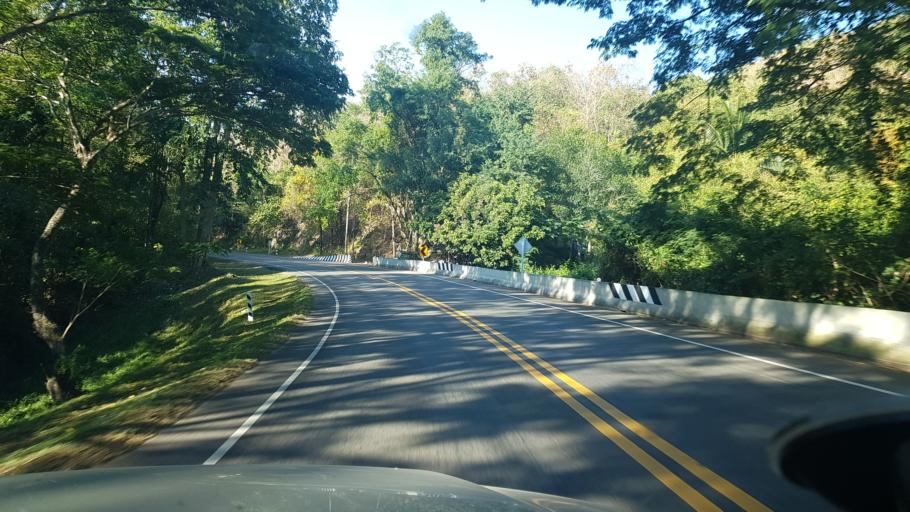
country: TH
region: Phetchabun
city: Lom Sak
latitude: 16.7477
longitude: 101.3959
